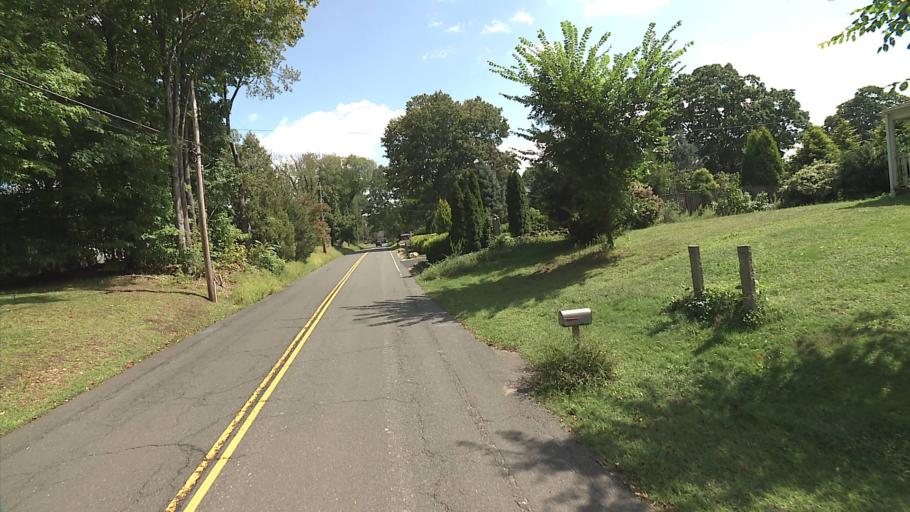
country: US
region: Connecticut
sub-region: Hartford County
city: Glastonbury Center
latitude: 41.6645
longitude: -72.6198
